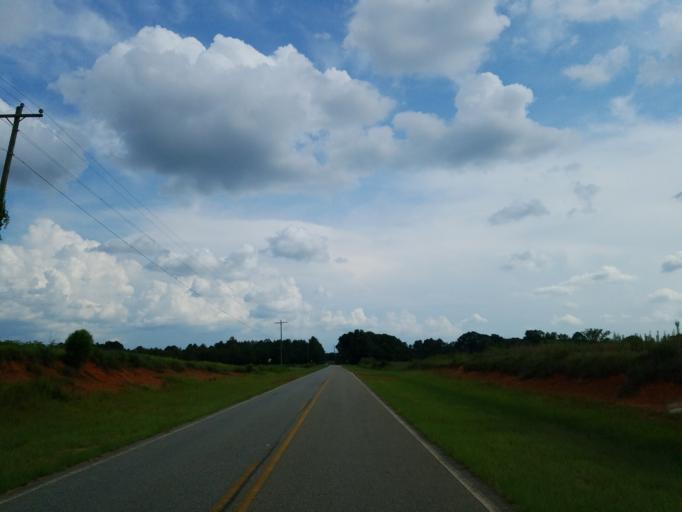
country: US
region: Georgia
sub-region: Dooly County
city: Unadilla
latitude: 32.2633
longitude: -83.7193
